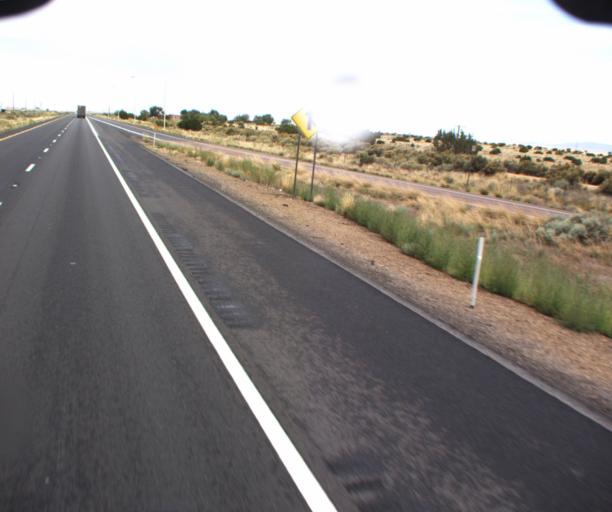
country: US
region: Arizona
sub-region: Coconino County
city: Flagstaff
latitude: 35.1603
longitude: -111.2693
